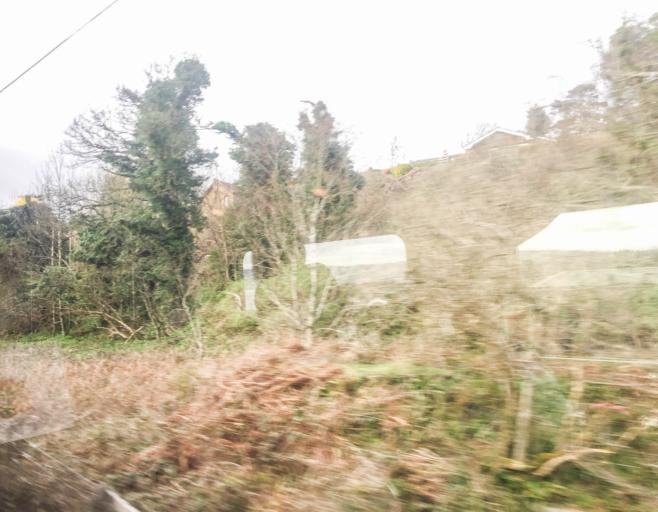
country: GB
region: Scotland
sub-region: West Dunbartonshire
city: Renton
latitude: 55.9475
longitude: -4.6059
